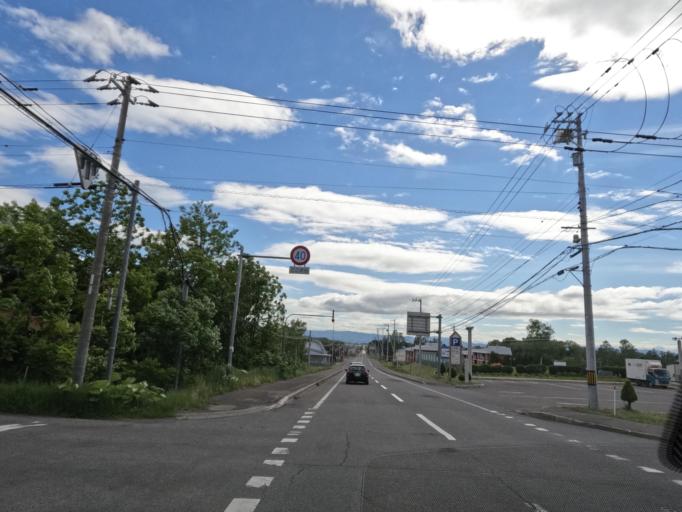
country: JP
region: Hokkaido
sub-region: Asahikawa-shi
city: Asahikawa
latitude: 43.8324
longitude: 142.5324
